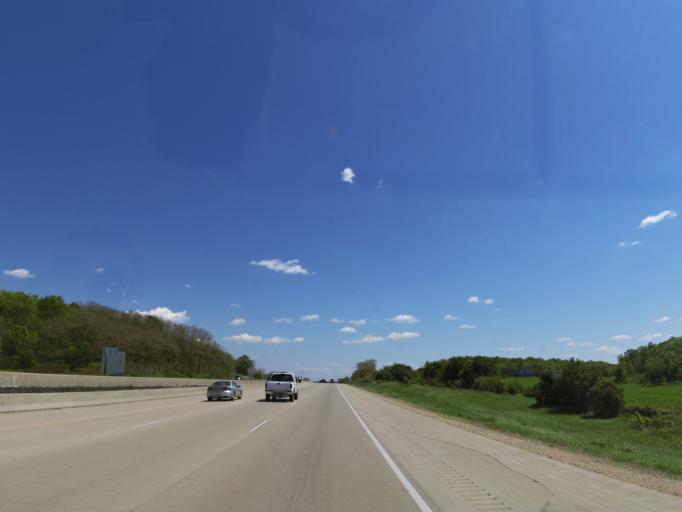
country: US
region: Wisconsin
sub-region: Columbia County
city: Lodi
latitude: 43.3214
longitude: -89.4469
